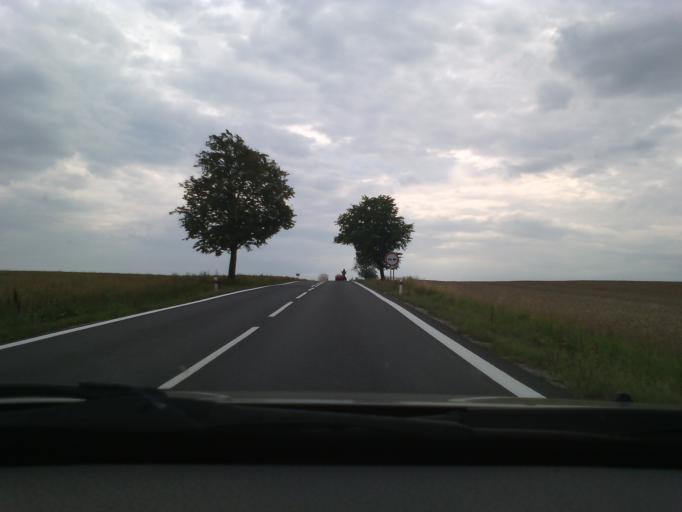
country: SK
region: Presovsky
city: Spisska Bela
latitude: 49.2028
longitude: 20.4722
